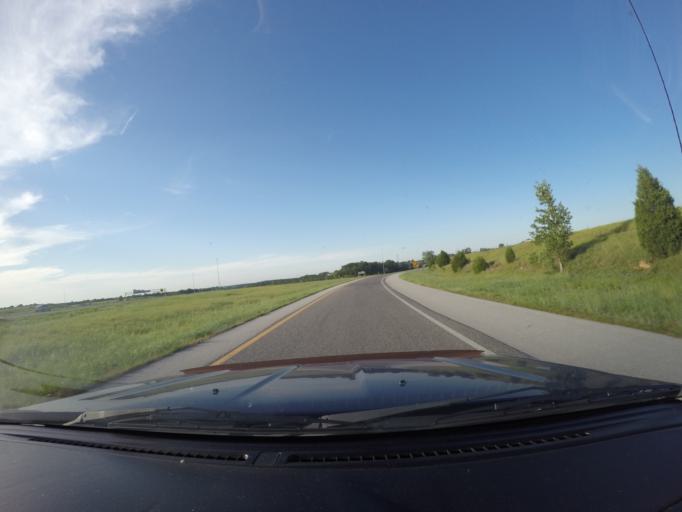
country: US
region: Kansas
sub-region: Wyandotte County
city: Edwardsville
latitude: 39.1397
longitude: -94.8189
